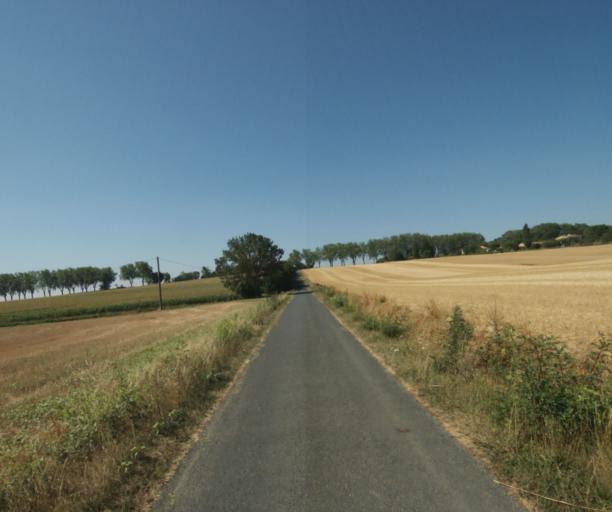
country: FR
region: Midi-Pyrenees
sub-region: Departement de la Haute-Garonne
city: Revel
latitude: 43.5043
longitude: 1.9551
